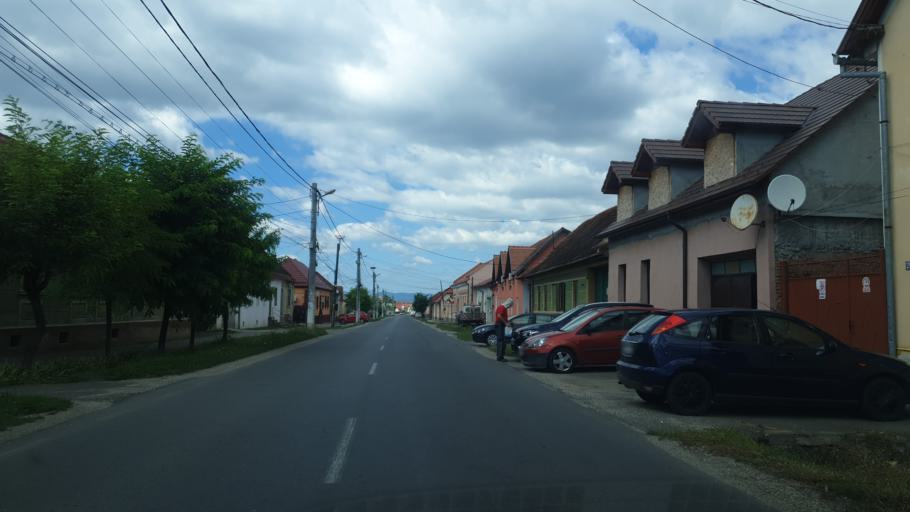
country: RO
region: Brasov
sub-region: Comuna Sanpetru
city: Sanpetru
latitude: 45.7133
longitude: 25.6325
